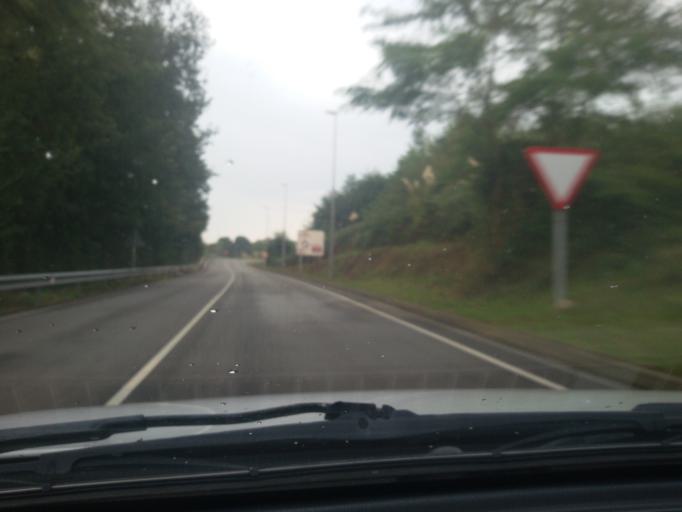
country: ES
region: Asturias
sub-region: Province of Asturias
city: Norena
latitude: 43.3734
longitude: -5.7249
